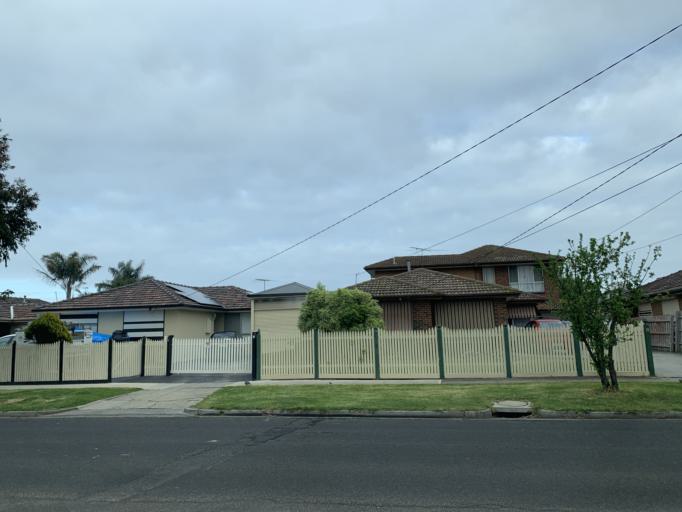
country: AU
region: Victoria
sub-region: Brimbank
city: Kealba
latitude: -37.7475
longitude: 144.8207
